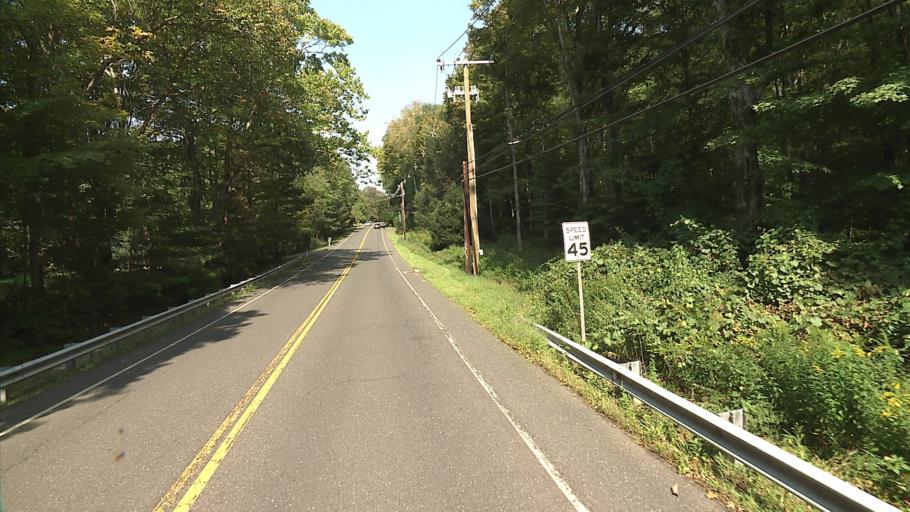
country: US
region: Connecticut
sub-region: New Haven County
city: Heritage Village
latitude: 41.4995
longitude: -73.2563
